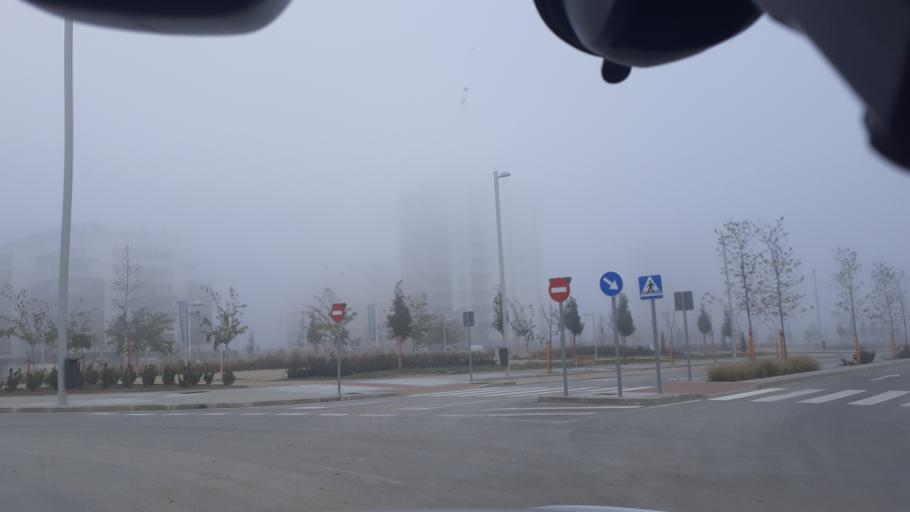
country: ES
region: Madrid
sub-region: Provincia de Madrid
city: Coslada
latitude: 40.3987
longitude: -3.5589
